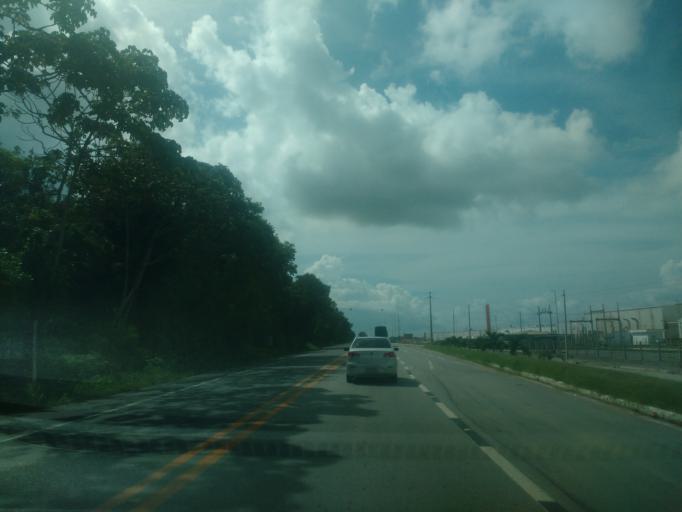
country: BR
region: Alagoas
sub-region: Marechal Deodoro
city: Marechal Deodoro
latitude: -9.6824
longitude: -35.8293
